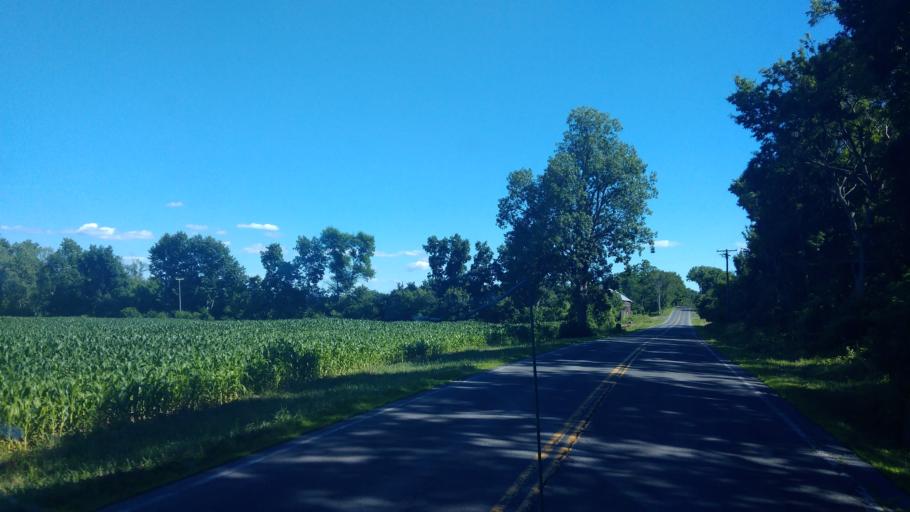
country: US
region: New York
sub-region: Seneca County
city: Seneca Falls
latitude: 42.9866
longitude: -76.8007
